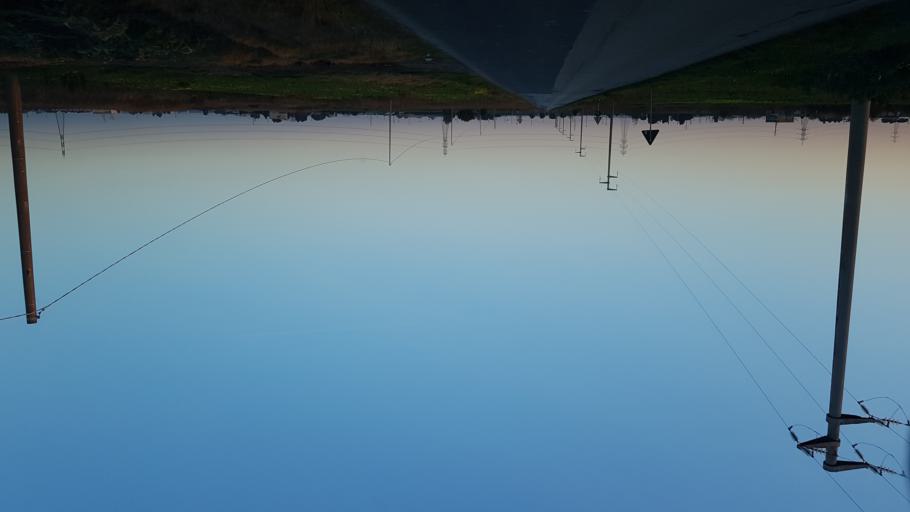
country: IT
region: Apulia
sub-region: Provincia di Brindisi
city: La Rosa
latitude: 40.5845
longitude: 17.9471
